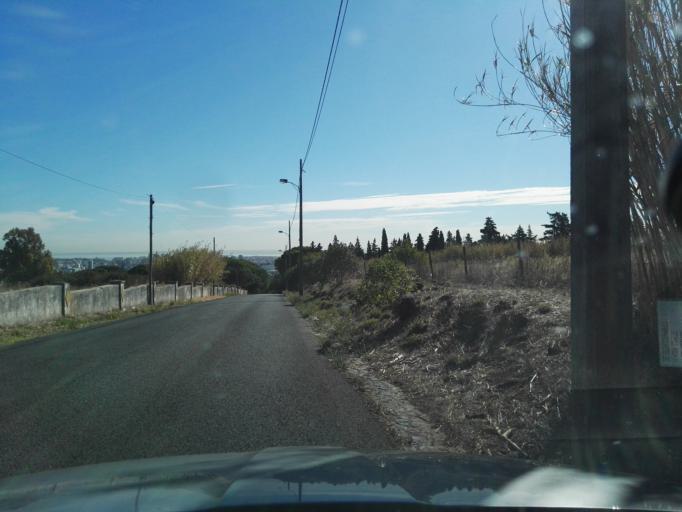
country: PT
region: Lisbon
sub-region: Odivelas
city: Pontinha
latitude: 38.7333
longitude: -9.1861
